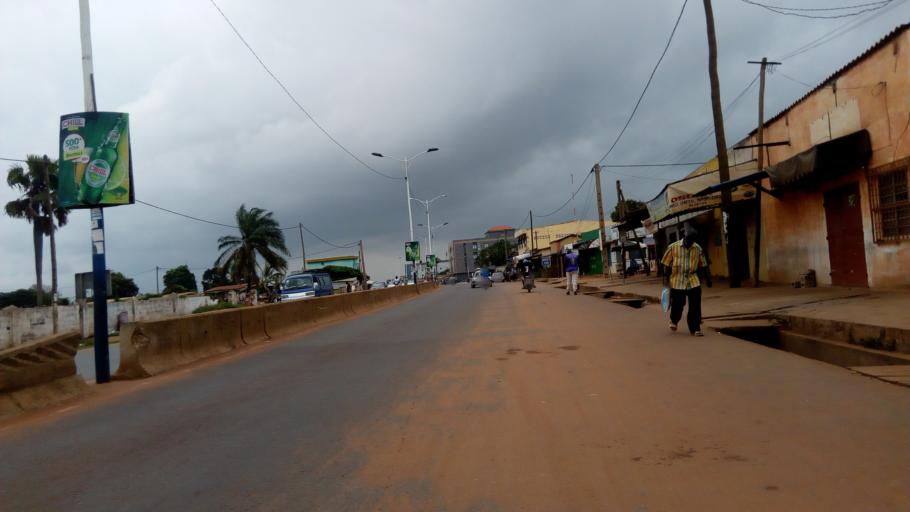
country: TG
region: Maritime
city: Lome
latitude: 6.2267
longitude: 1.2109
